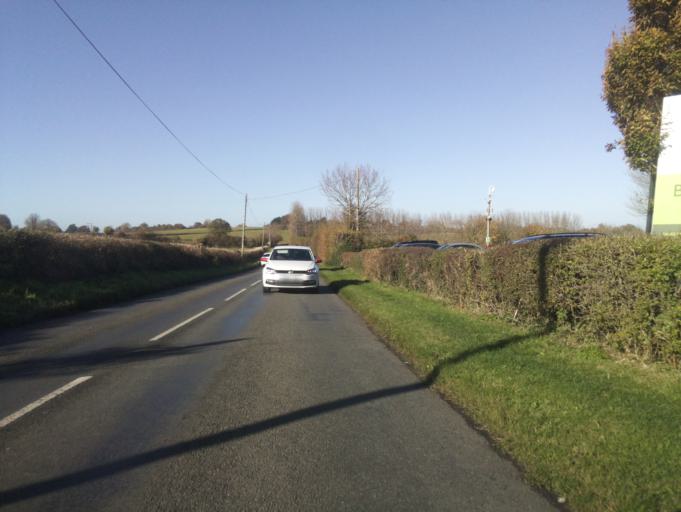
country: GB
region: England
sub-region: Somerset
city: Yeovil
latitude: 50.9576
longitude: -2.6539
